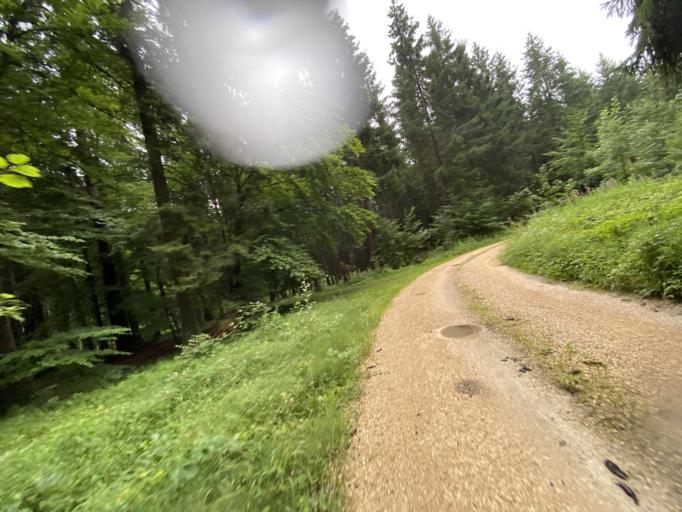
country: DE
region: Baden-Wuerttemberg
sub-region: Tuebingen Region
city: Sigmaringen
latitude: 48.1180
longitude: 9.2341
